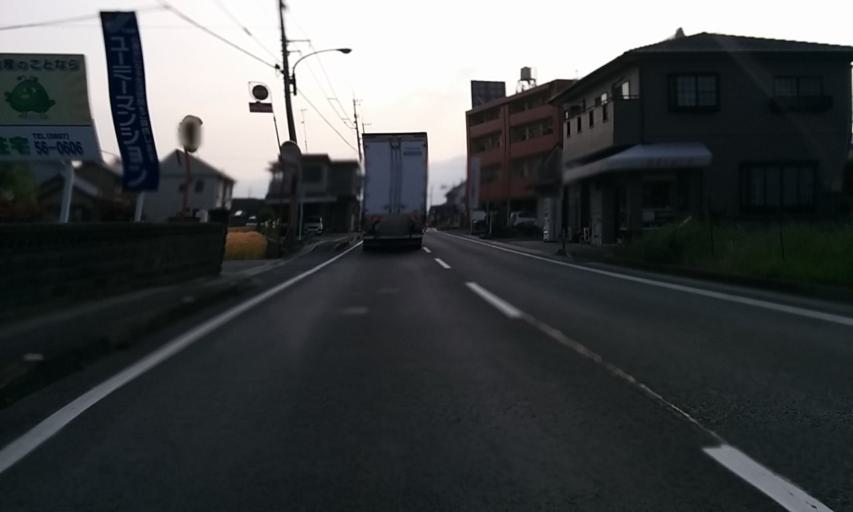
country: JP
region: Ehime
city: Saijo
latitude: 33.8954
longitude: 133.0982
